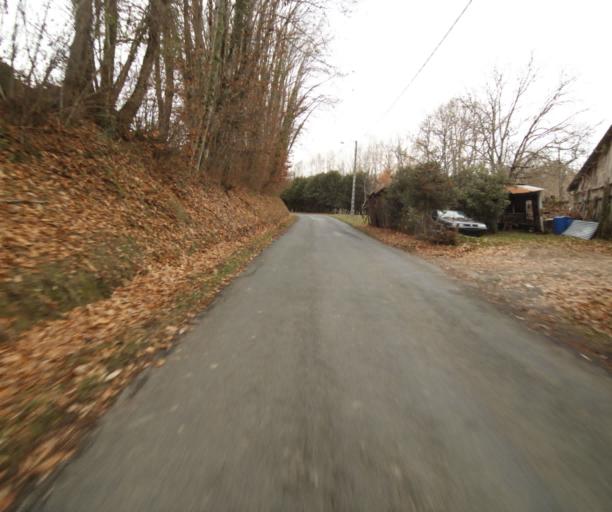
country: FR
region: Limousin
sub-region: Departement de la Correze
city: Chameyrat
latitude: 45.2488
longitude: 1.6845
